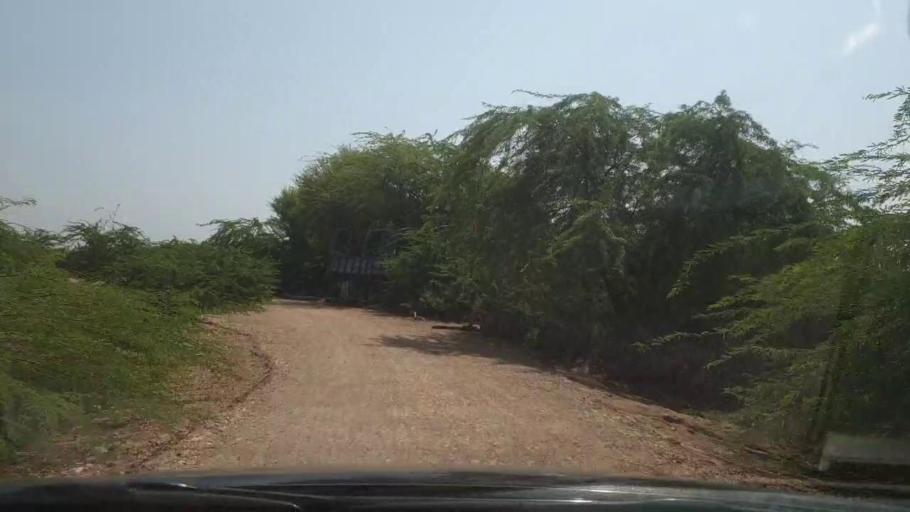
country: PK
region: Sindh
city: Tando Bago
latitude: 24.7990
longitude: 69.1562
